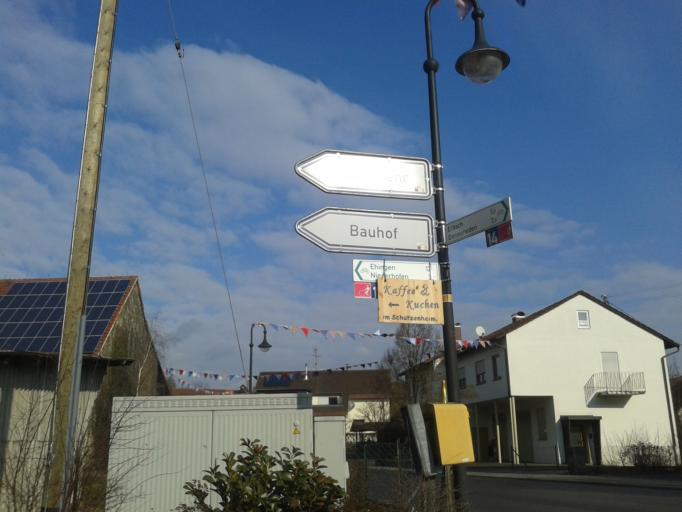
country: DE
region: Baden-Wuerttemberg
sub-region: Tuebingen Region
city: Oberdischingen
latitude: 48.3020
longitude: 9.8296
